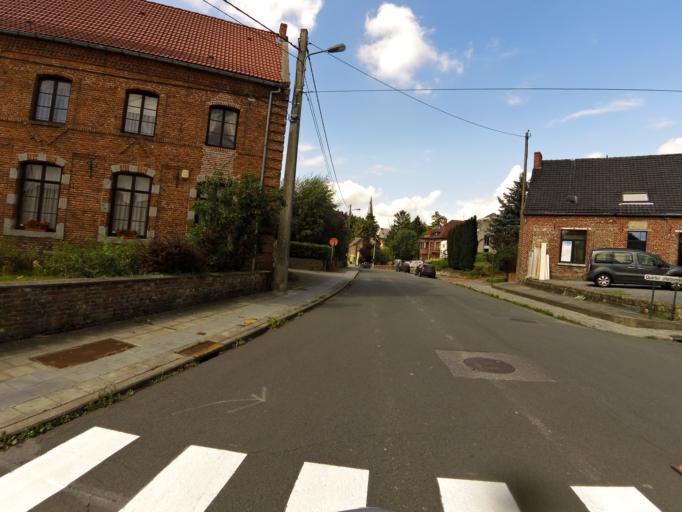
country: BE
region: Wallonia
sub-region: Province du Hainaut
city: Saint-Ghislain
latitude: 50.4833
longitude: 3.8376
